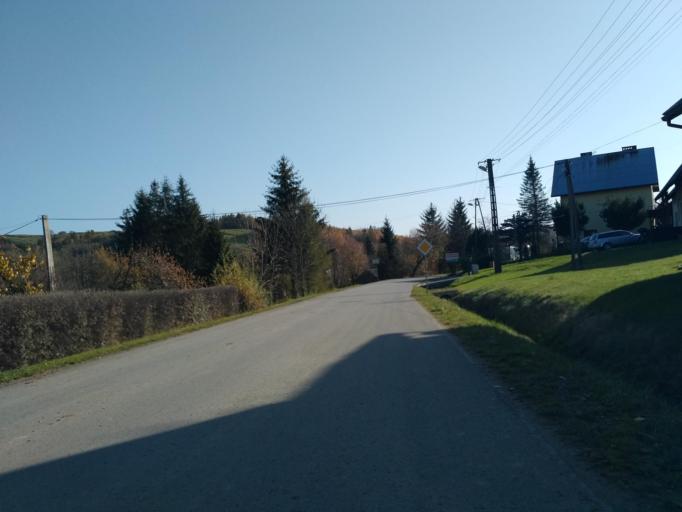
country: PL
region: Subcarpathian Voivodeship
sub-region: Powiat brzozowski
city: Nozdrzec
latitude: 49.8020
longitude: 22.1716
